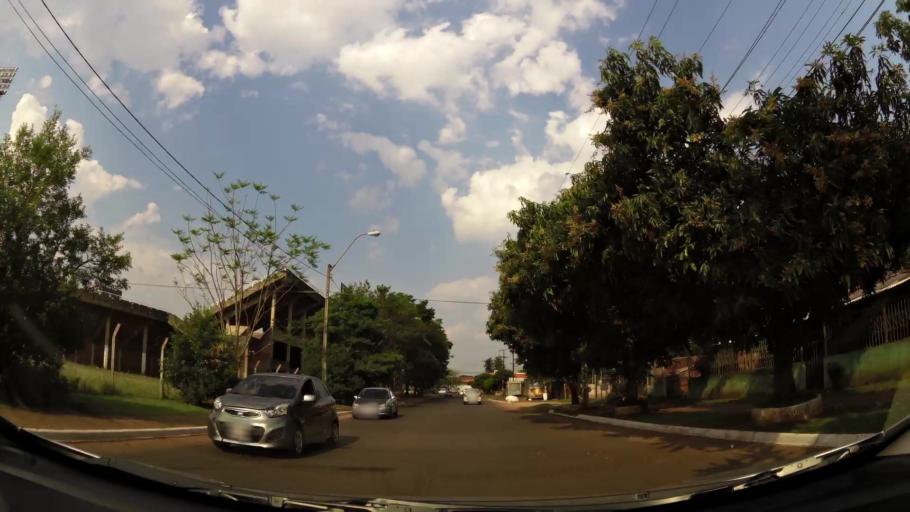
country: PY
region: Alto Parana
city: Presidente Franco
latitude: -25.5282
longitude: -54.6127
